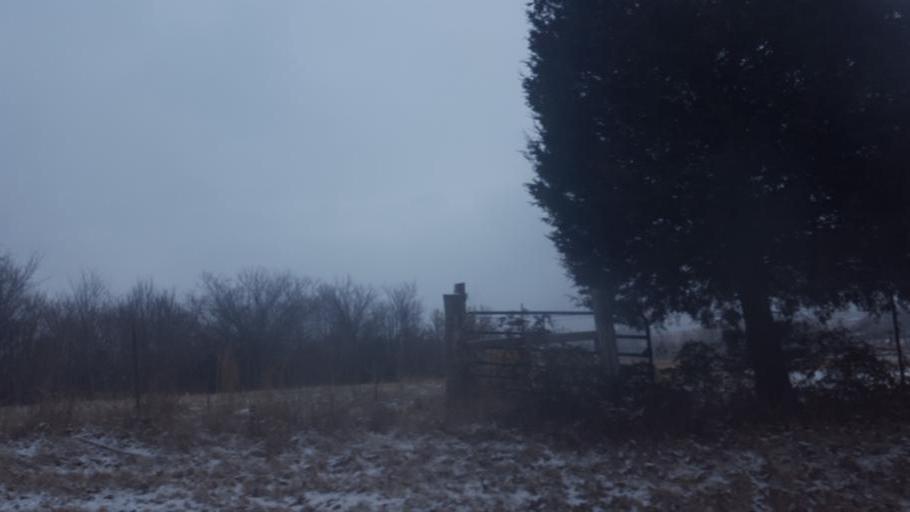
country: US
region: Kentucky
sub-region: Crittenden County
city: Marion
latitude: 37.4051
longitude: -88.0255
